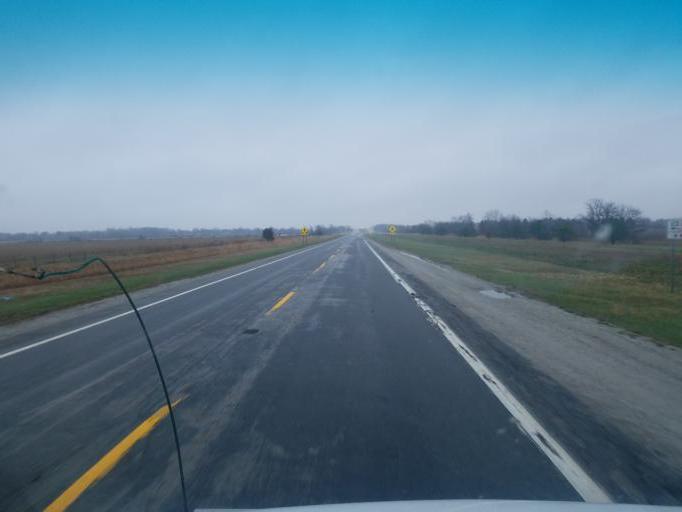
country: US
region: Ohio
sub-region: Wood County
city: Bowling Green
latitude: 41.3495
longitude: -83.6747
